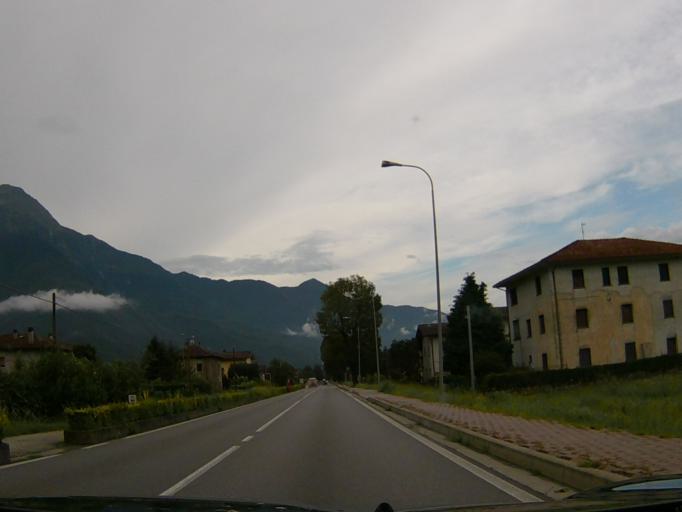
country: IT
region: Lombardy
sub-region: Provincia di Sondrio
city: Dubino
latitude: 46.1652
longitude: 9.4266
